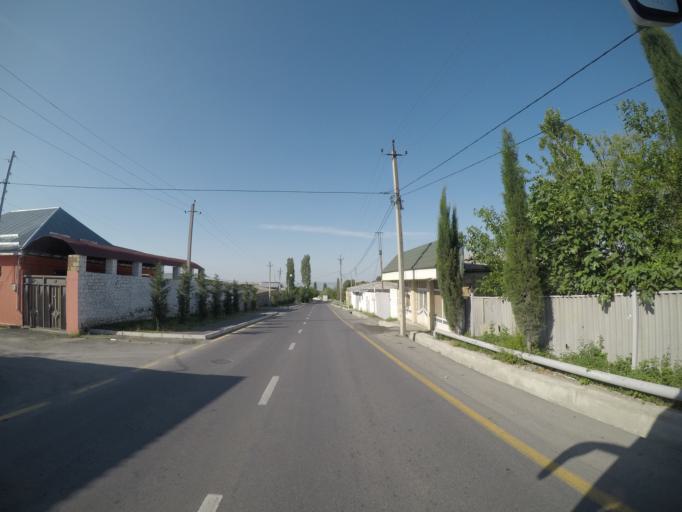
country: AZ
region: Shaki City
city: Sheki
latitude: 41.2127
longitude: 47.1671
